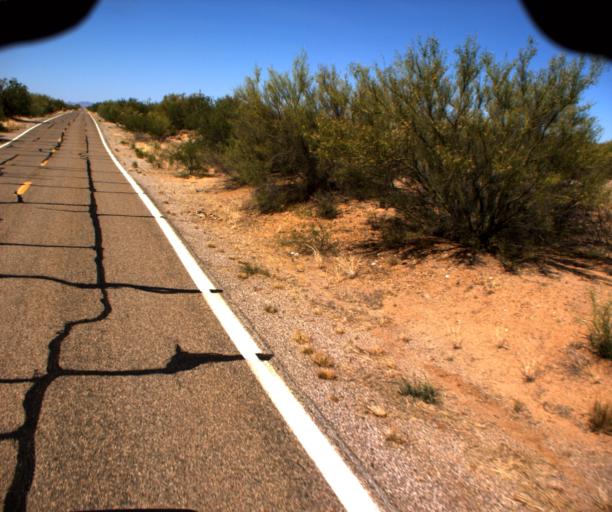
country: US
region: Arizona
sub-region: Pima County
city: Three Points
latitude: 31.9916
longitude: -111.3680
